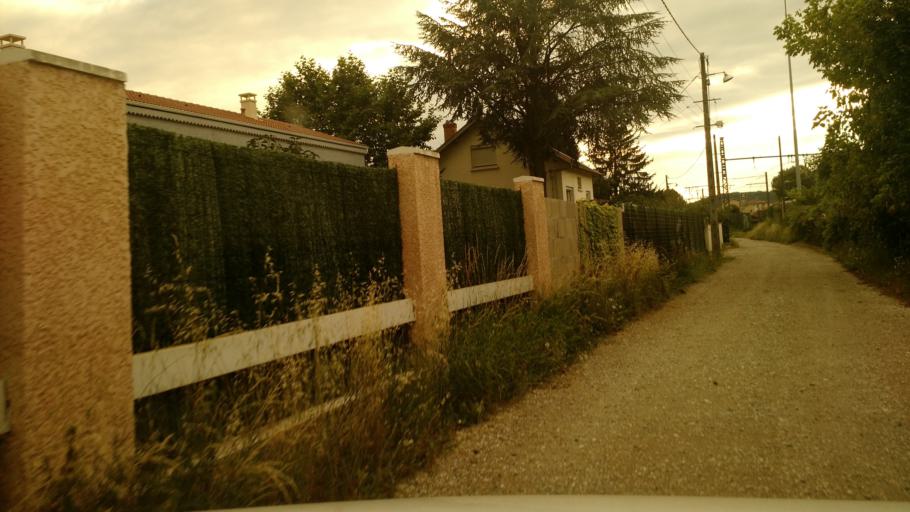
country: FR
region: Rhone-Alpes
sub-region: Departement de l'Ain
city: Montluel
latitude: 45.8483
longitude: 5.0616
